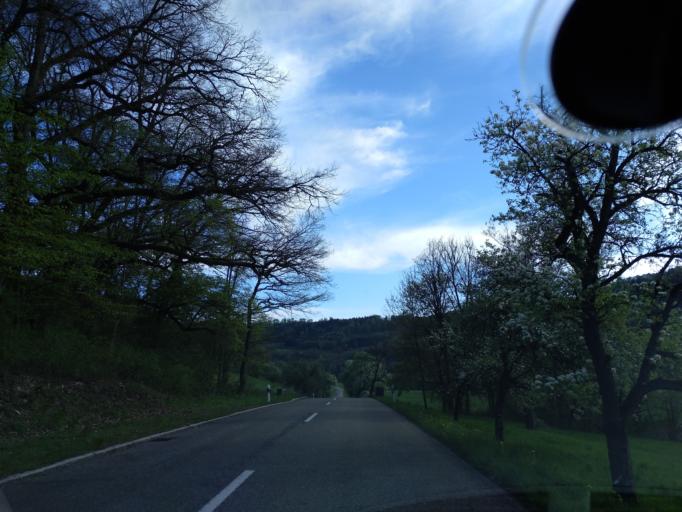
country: DE
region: Baden-Wuerttemberg
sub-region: Regierungsbezirk Stuttgart
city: Braunsbach
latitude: 49.2147
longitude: 9.7787
